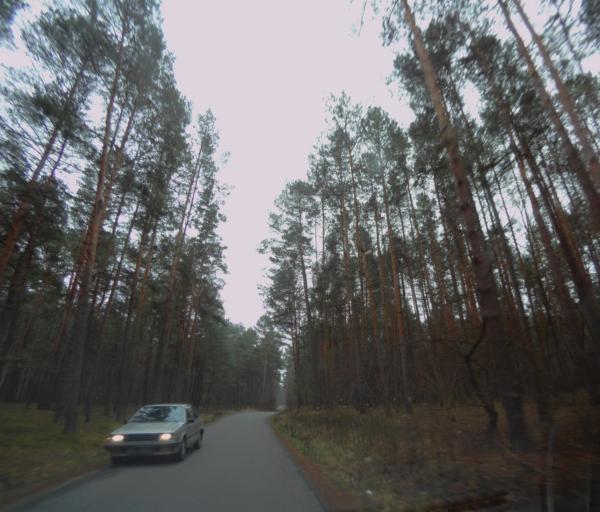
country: PL
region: Subcarpathian Voivodeship
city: Nowa Sarzyna
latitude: 50.3055
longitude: 22.3462
